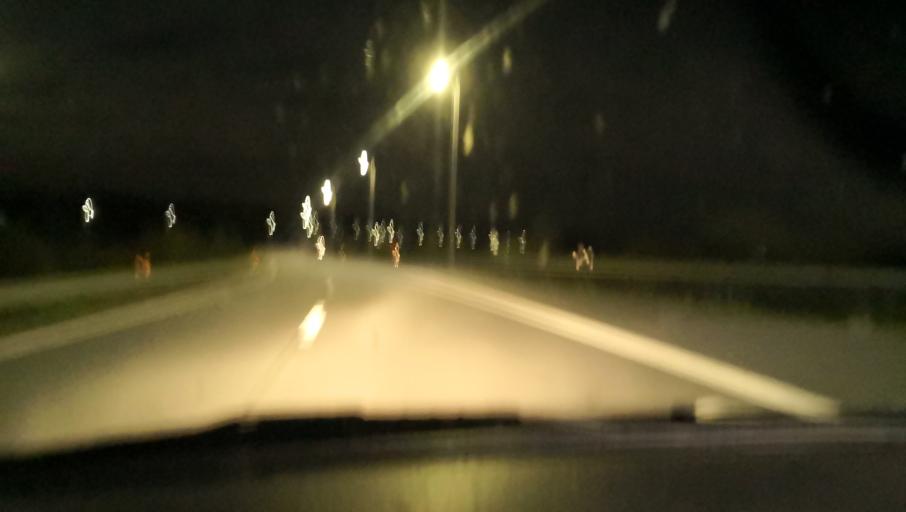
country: PT
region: Evora
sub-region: Vendas Novas
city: Vendas Novas
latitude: 38.6019
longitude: -8.6445
